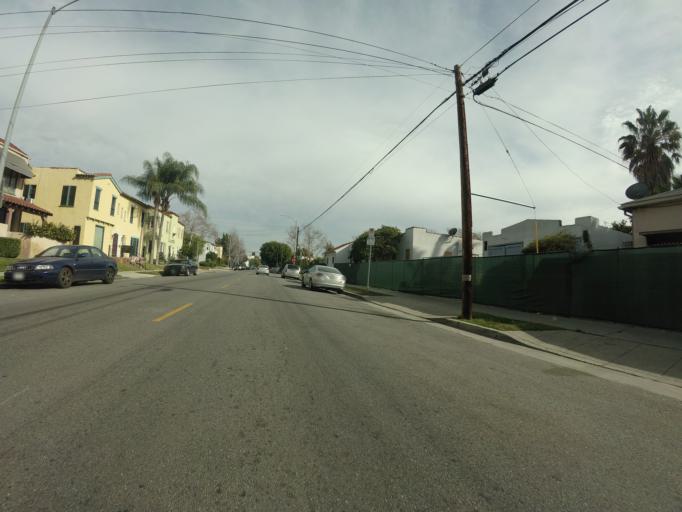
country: US
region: California
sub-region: Los Angeles County
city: Hollywood
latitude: 34.0871
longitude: -118.3424
